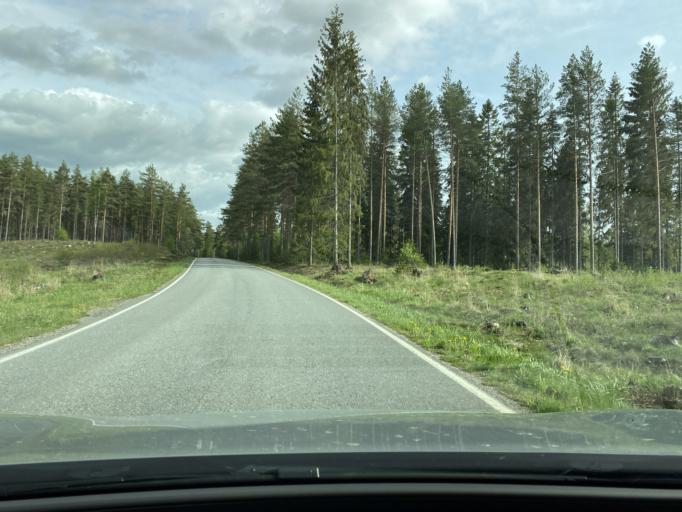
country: FI
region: Varsinais-Suomi
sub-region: Salo
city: Kiikala
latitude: 60.5138
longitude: 23.5311
